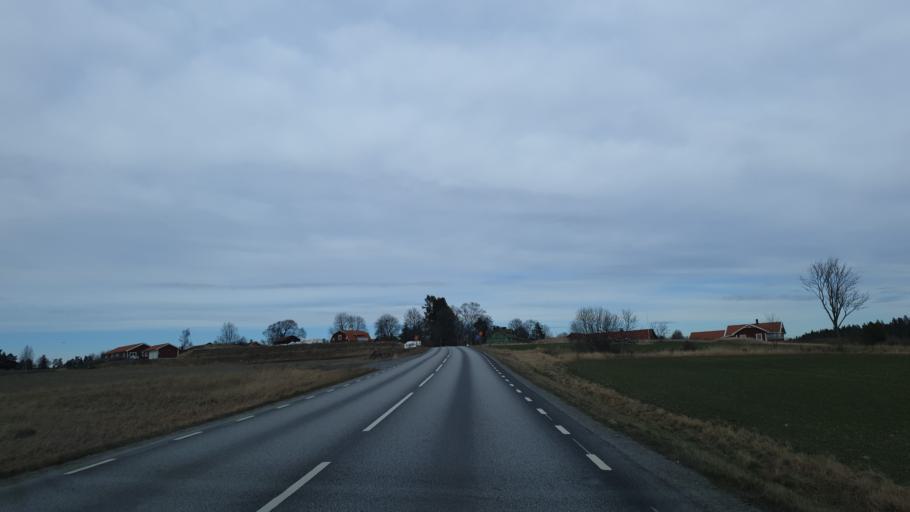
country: SE
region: Stockholm
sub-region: Osterakers Kommun
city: Akersberga
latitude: 59.5689
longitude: 18.2610
